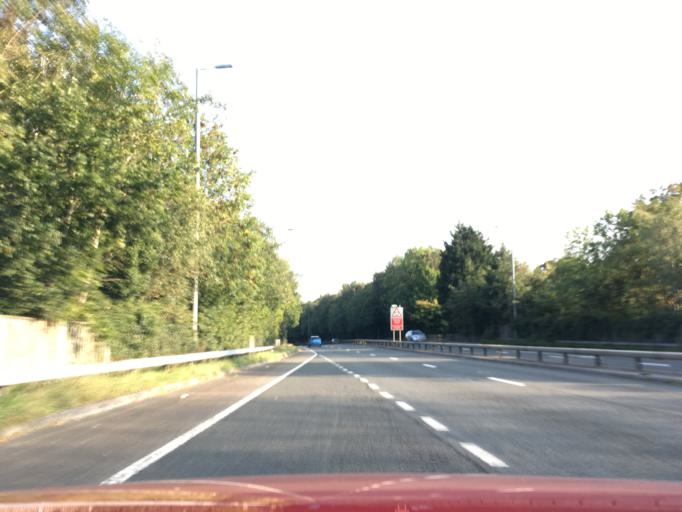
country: GB
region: Wales
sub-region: Torfaen County Borough
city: Pontypool
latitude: 51.6961
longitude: -3.0268
